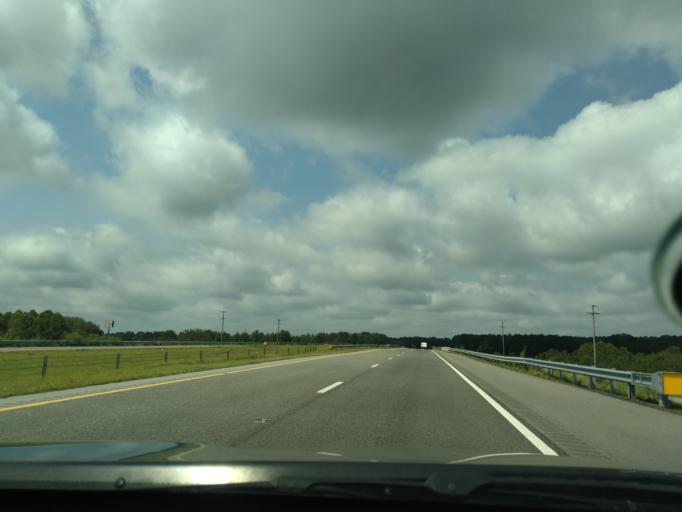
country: US
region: North Carolina
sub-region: Martin County
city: Robersonville
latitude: 35.8370
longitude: -77.2510
